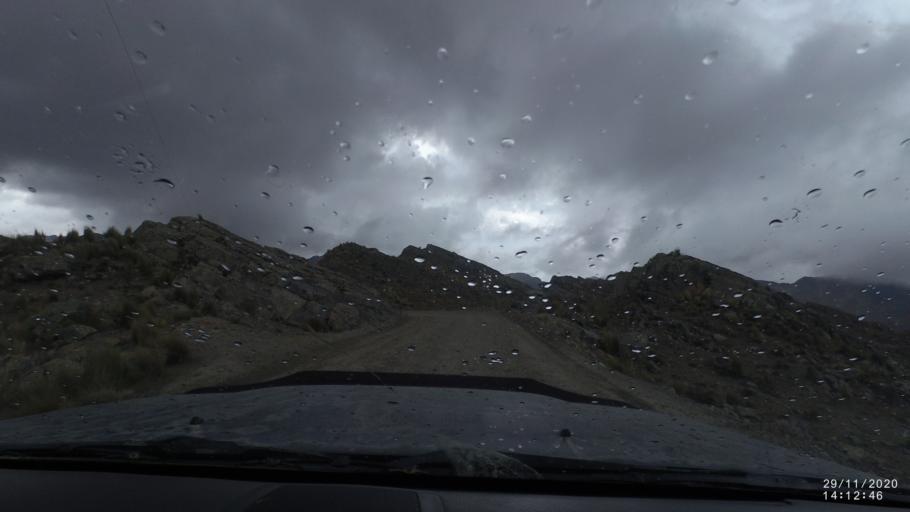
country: BO
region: Cochabamba
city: Sipe Sipe
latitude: -17.2403
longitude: -66.3946
